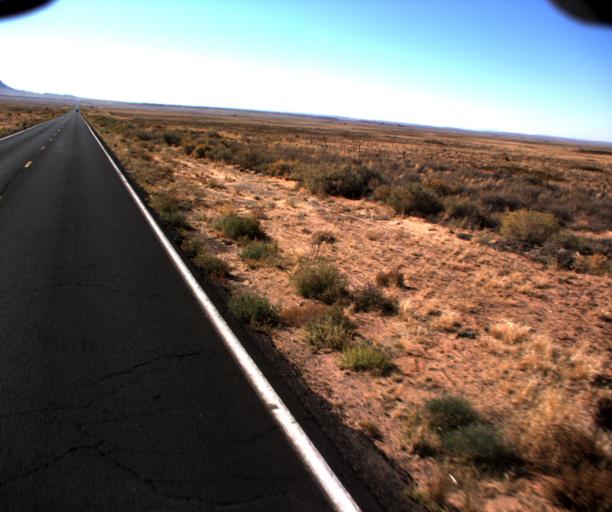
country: US
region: Arizona
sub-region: Navajo County
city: Dilkon
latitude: 35.3884
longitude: -110.4257
